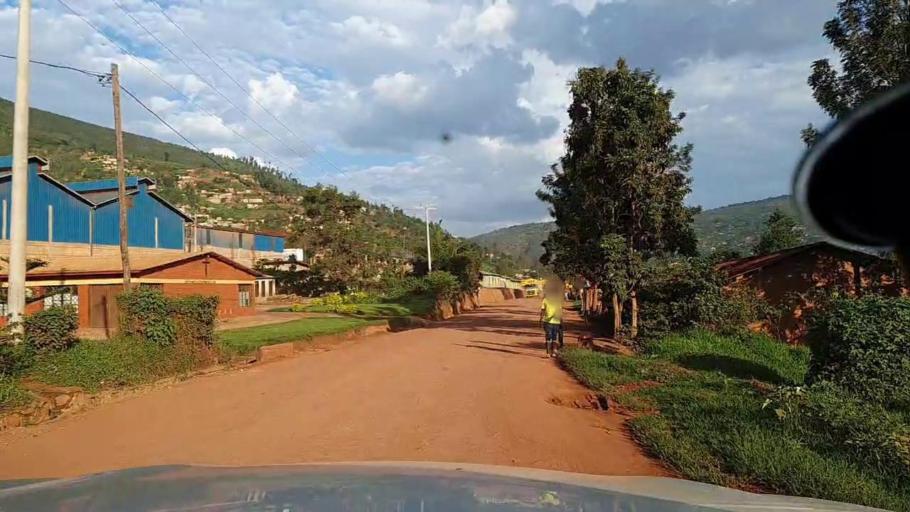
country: RW
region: Kigali
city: Kigali
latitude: -1.9439
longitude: 30.0054
